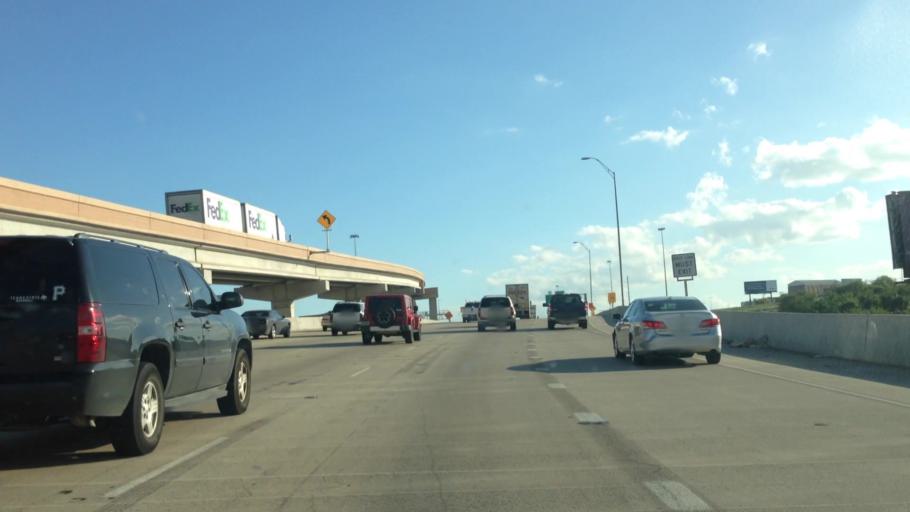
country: US
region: Texas
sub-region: Tarrant County
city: Fort Worth
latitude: 32.7601
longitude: -97.3187
